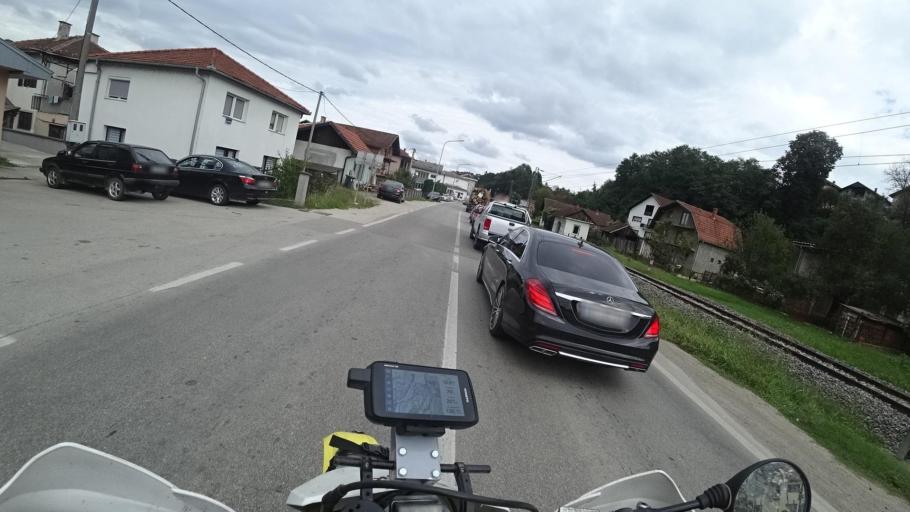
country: BA
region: Republika Srpska
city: Bosanski Novi
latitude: 45.0455
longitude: 16.3748
